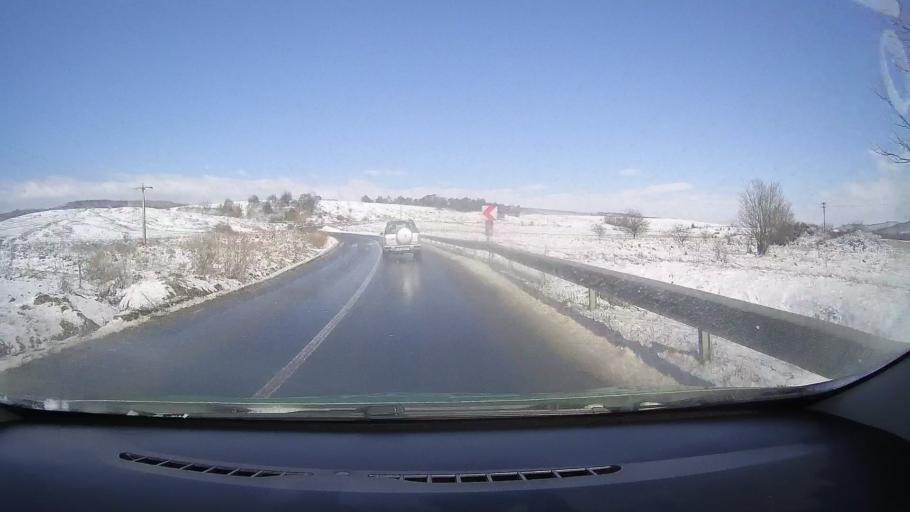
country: RO
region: Sibiu
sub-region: Comuna Rosia
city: Rosia
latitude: 45.8097
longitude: 24.3605
